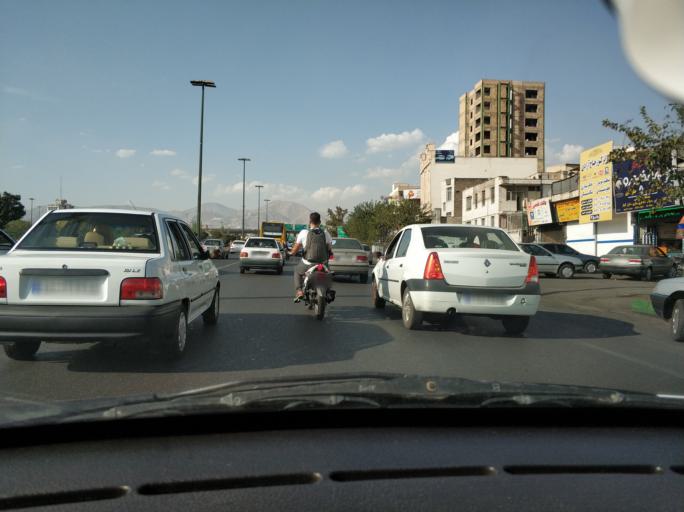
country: IR
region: Tehran
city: Tehran
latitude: 35.7073
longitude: 51.3372
